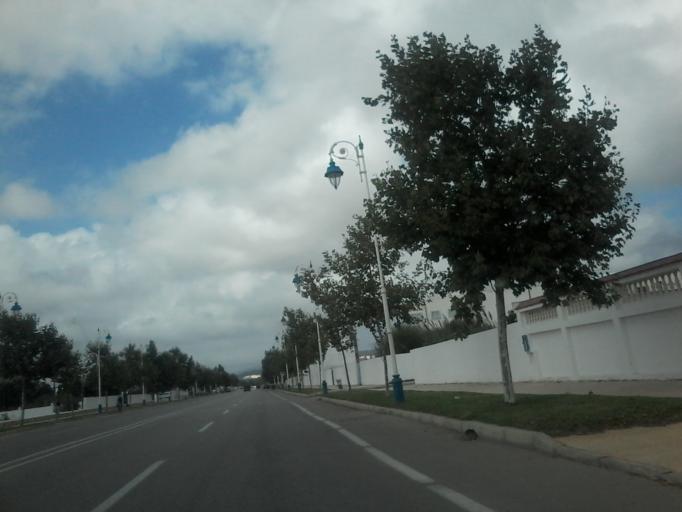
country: MA
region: Tanger-Tetouan
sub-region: Tetouan
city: Martil
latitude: 35.6357
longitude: -5.2882
